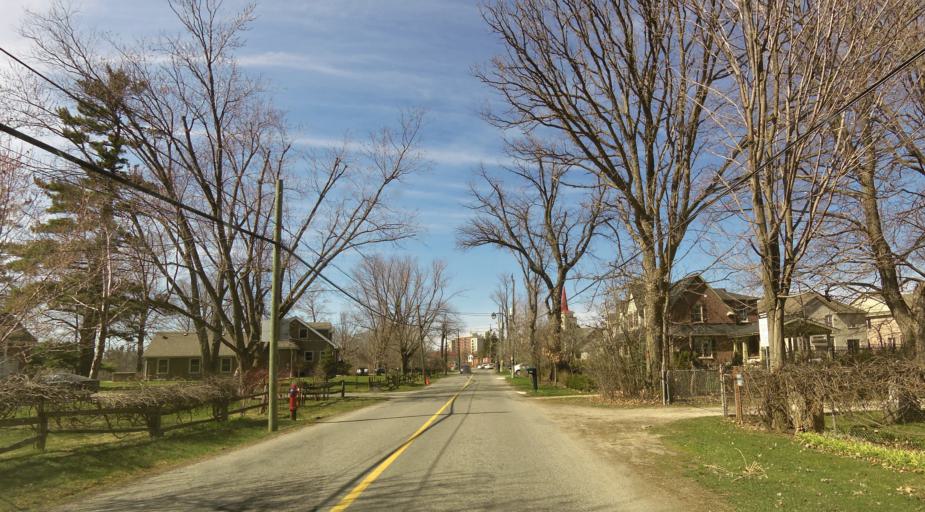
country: CA
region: Ontario
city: Brampton
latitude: 43.6385
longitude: -79.7612
